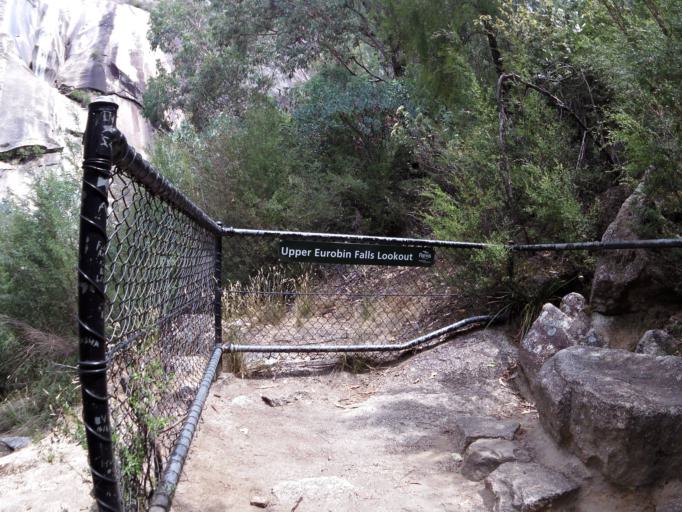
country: AU
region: Victoria
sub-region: Alpine
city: Mount Beauty
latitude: -36.7190
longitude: 146.8367
